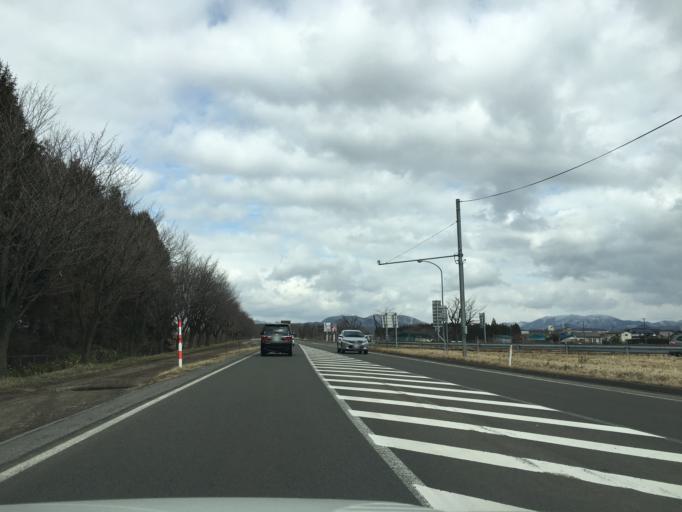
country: JP
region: Akita
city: Hanawa
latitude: 40.2569
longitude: 140.7617
